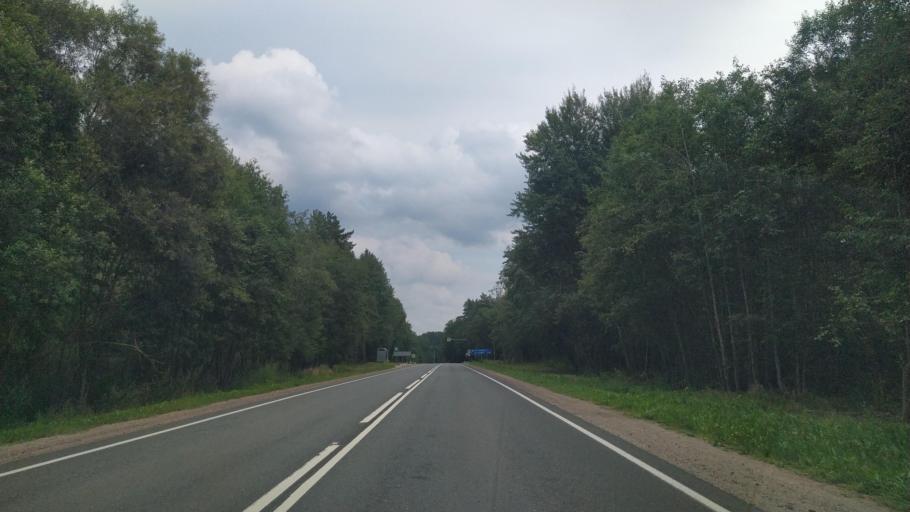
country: RU
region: Pskov
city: Pskov
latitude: 57.8330
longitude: 28.5264
